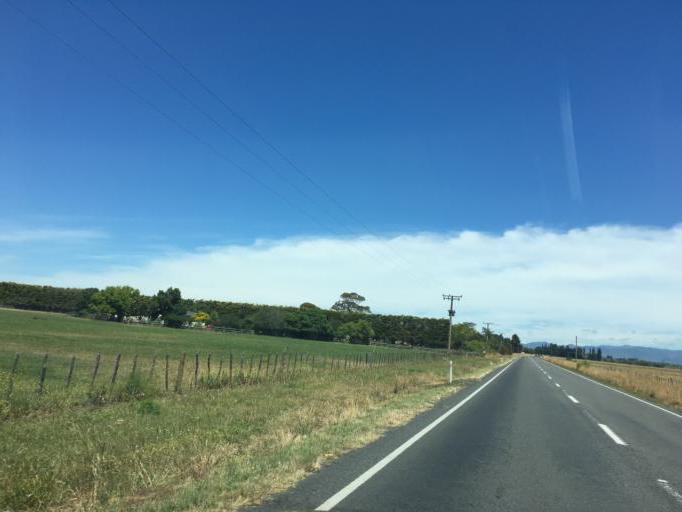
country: NZ
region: Hawke's Bay
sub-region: Hastings District
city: Hastings
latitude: -39.9973
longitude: 176.4157
